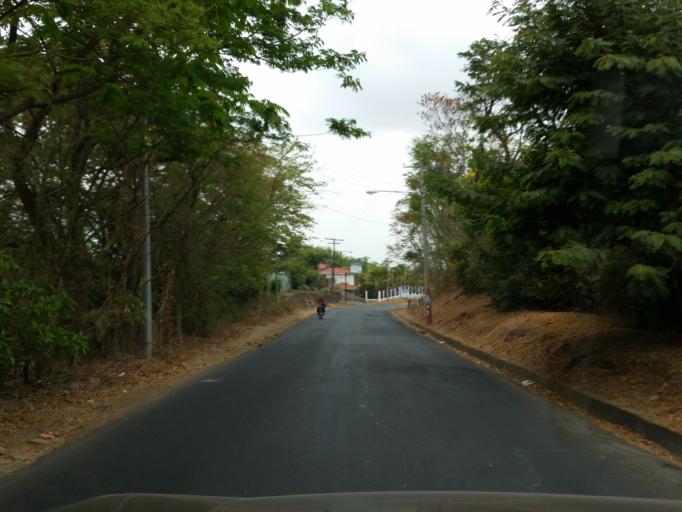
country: NI
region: Managua
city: Managua
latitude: 12.0927
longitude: -86.2660
